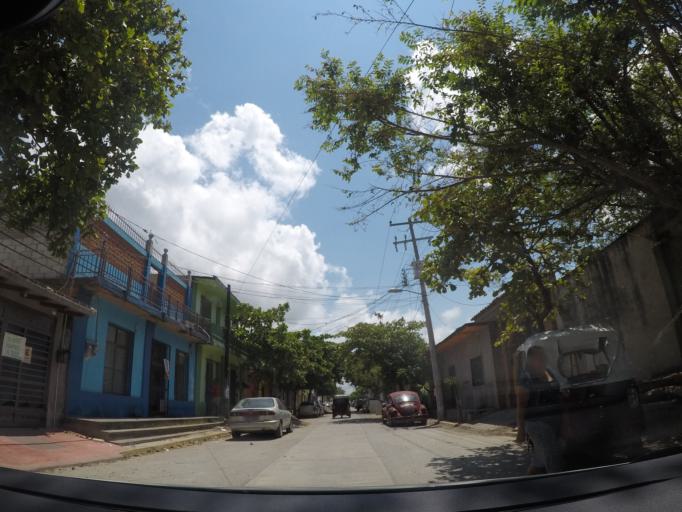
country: MX
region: Oaxaca
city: Juchitan de Zaragoza
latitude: 16.4340
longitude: -95.0162
